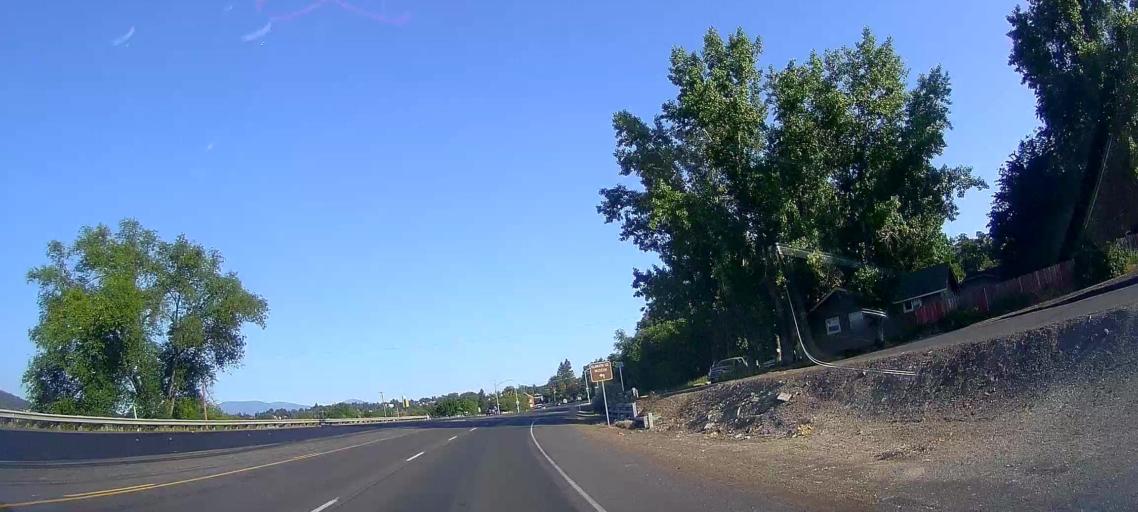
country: US
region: Oregon
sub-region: Klamath County
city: Klamath Falls
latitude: 42.2271
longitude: -121.7645
